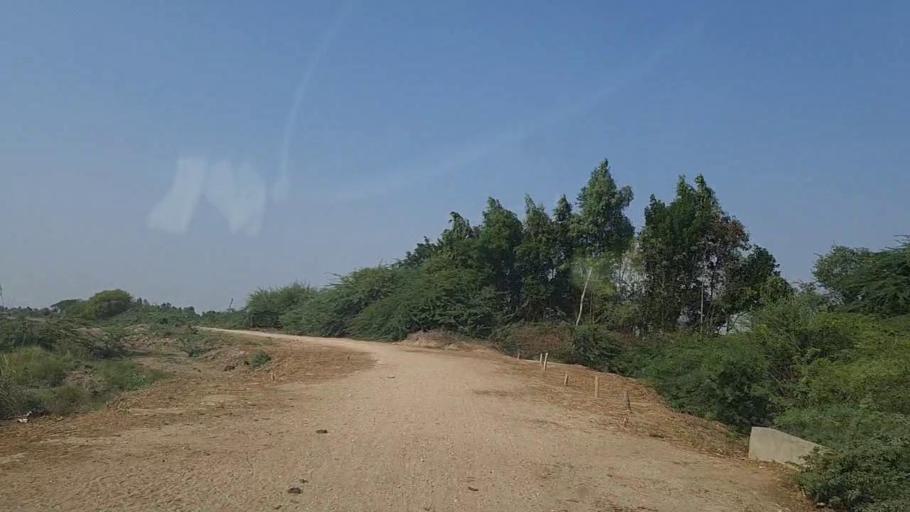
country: PK
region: Sindh
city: Mirpur Sakro
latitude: 24.5630
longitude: 67.8295
